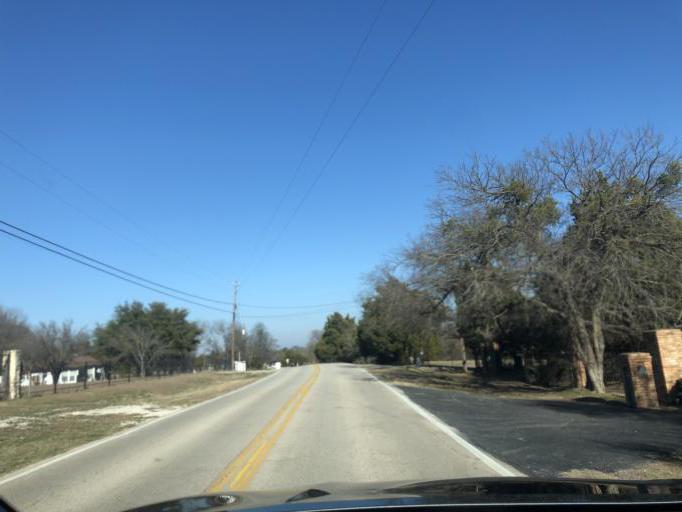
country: US
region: Texas
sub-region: Dallas County
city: Cedar Hill
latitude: 32.6162
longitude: -96.9349
